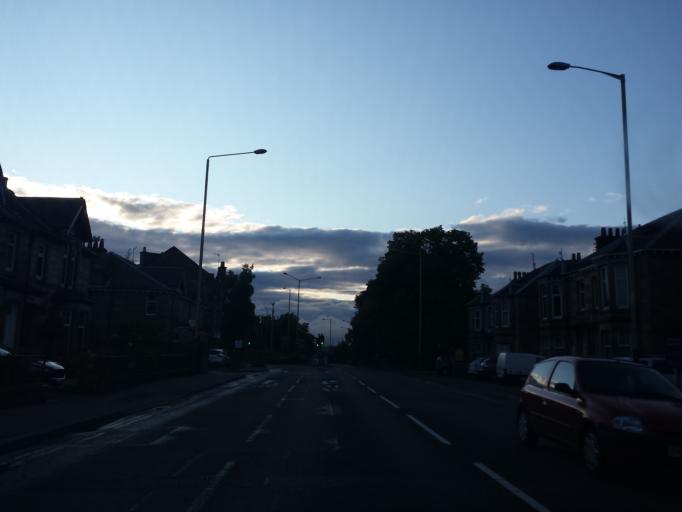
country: GB
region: Scotland
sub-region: Perth and Kinross
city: Perth
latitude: 56.4029
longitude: -3.4416
